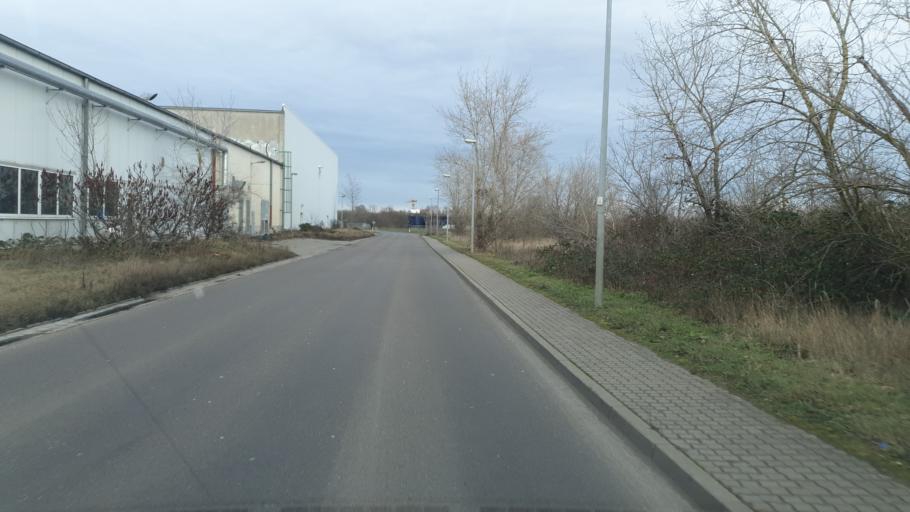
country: DE
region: Saxony
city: Kitzen
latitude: 51.2488
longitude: 12.2741
